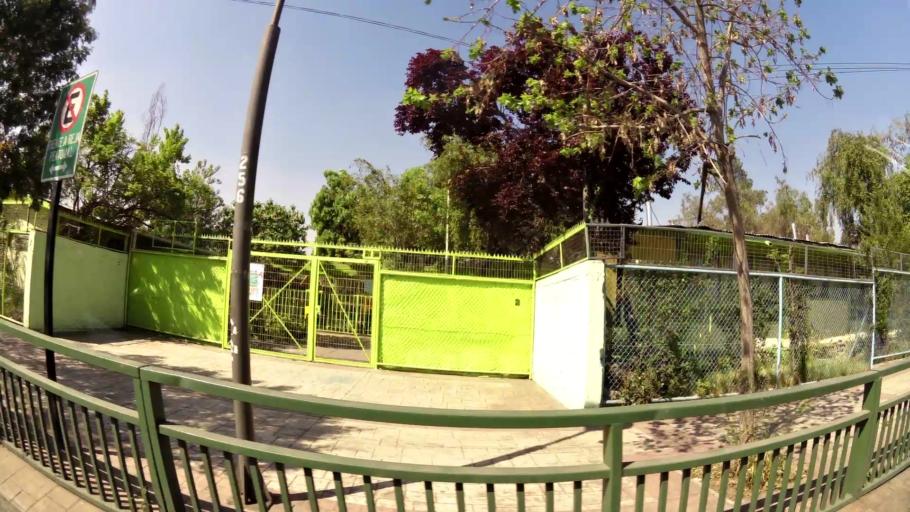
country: CL
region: Santiago Metropolitan
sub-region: Provincia de Santiago
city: La Pintana
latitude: -33.5459
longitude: -70.6151
